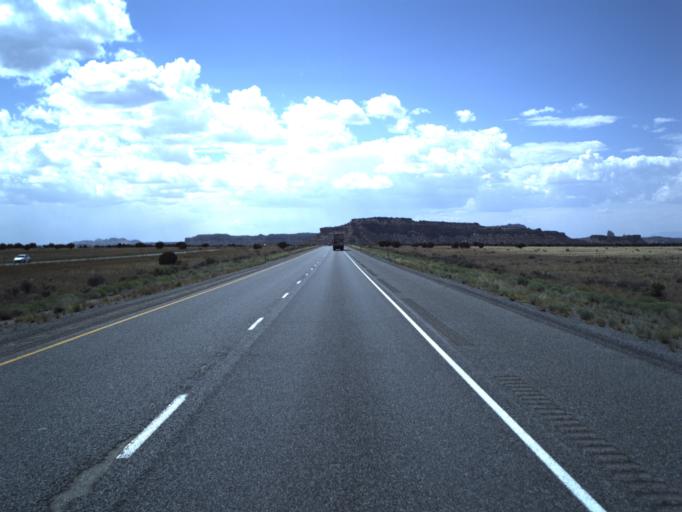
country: US
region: Utah
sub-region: Emery County
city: Castle Dale
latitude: 38.8929
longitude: -110.6299
